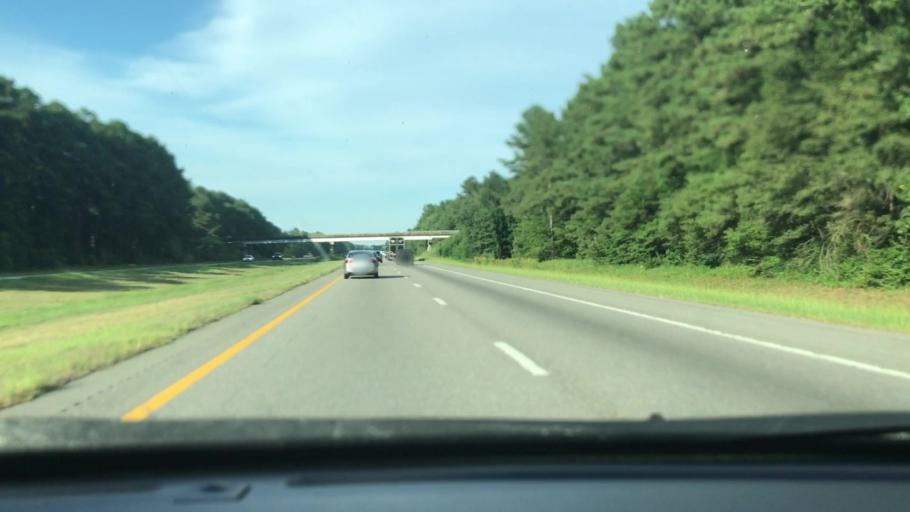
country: US
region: North Carolina
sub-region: Robeson County
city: Fairmont
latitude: 34.5679
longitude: -79.1670
